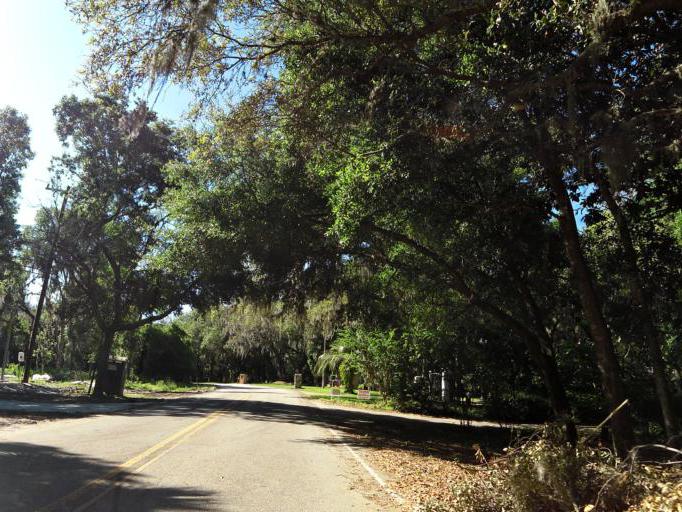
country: US
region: Florida
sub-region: Duval County
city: Atlantic Beach
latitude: 30.3856
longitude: -81.4890
